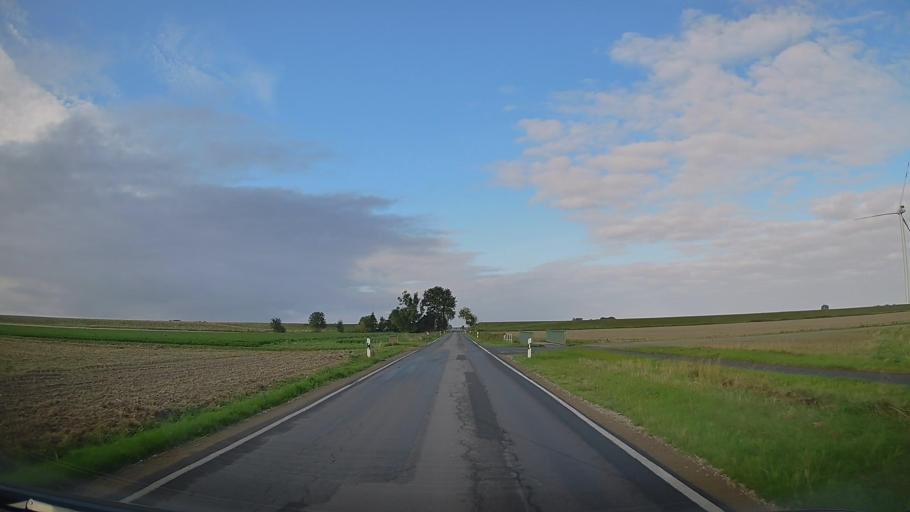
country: DE
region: Schleswig-Holstein
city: Breklum
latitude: 54.5718
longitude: 8.9439
